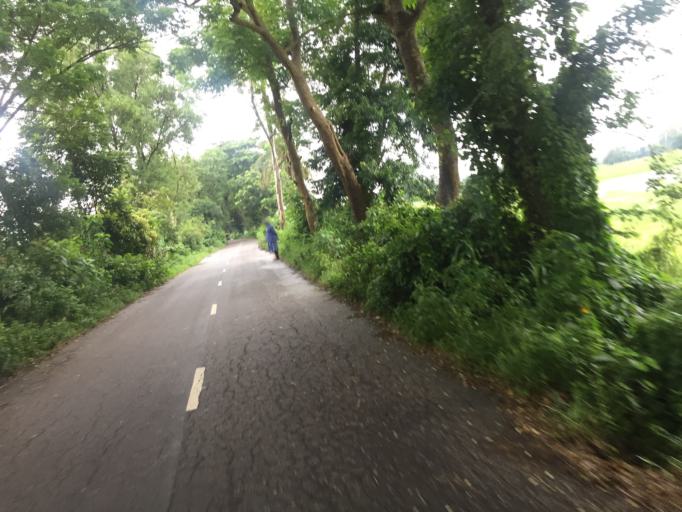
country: BD
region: Dhaka
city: Narayanganj
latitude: 23.5217
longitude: 90.4711
